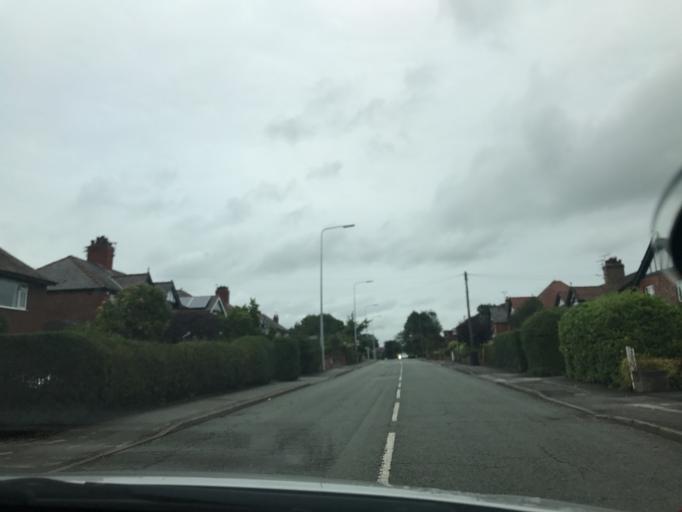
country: GB
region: England
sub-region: Cheshire West and Chester
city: Northwich
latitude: 53.2246
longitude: -2.5096
